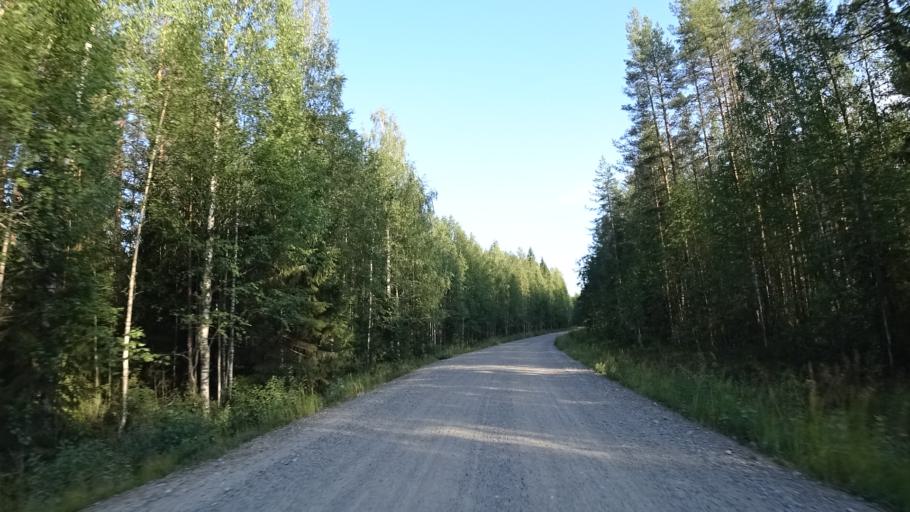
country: FI
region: North Karelia
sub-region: Joensuu
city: Ilomantsi
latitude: 63.1355
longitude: 30.7065
